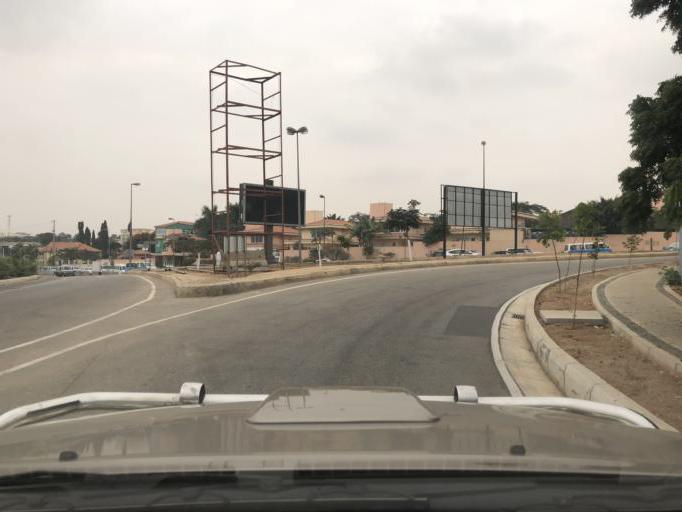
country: AO
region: Luanda
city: Luanda
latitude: -8.8928
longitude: 13.1774
